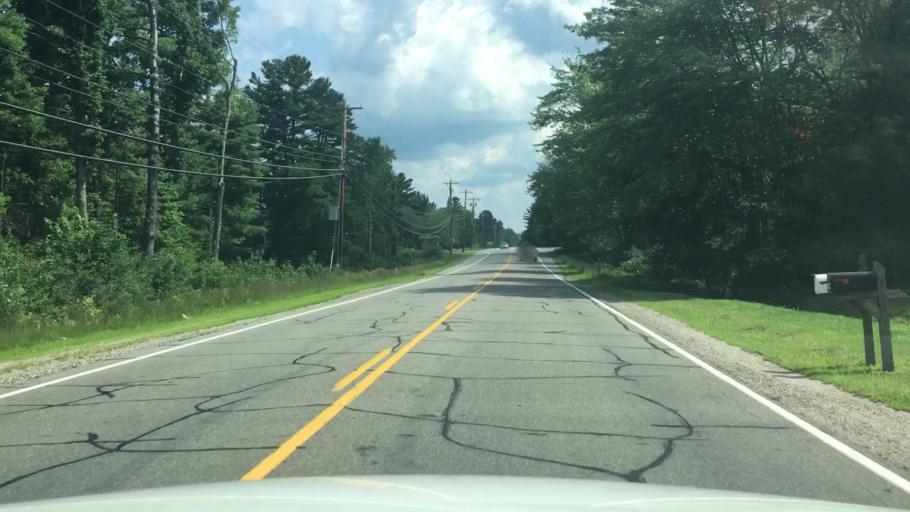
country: US
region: New Hampshire
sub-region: Rockingham County
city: Auburn
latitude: 42.9546
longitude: -71.3550
